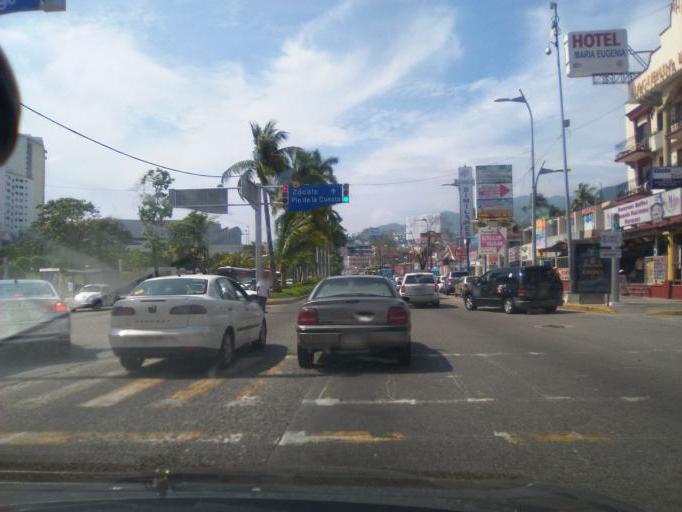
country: MX
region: Guerrero
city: Acapulco de Juarez
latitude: 16.8605
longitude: -99.8744
